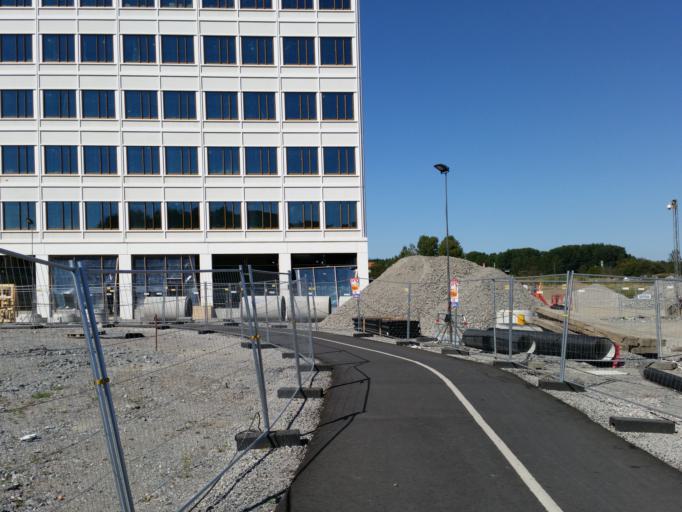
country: SE
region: Stockholm
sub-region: Solna Kommun
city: Solna
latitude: 59.3811
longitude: 18.0017
